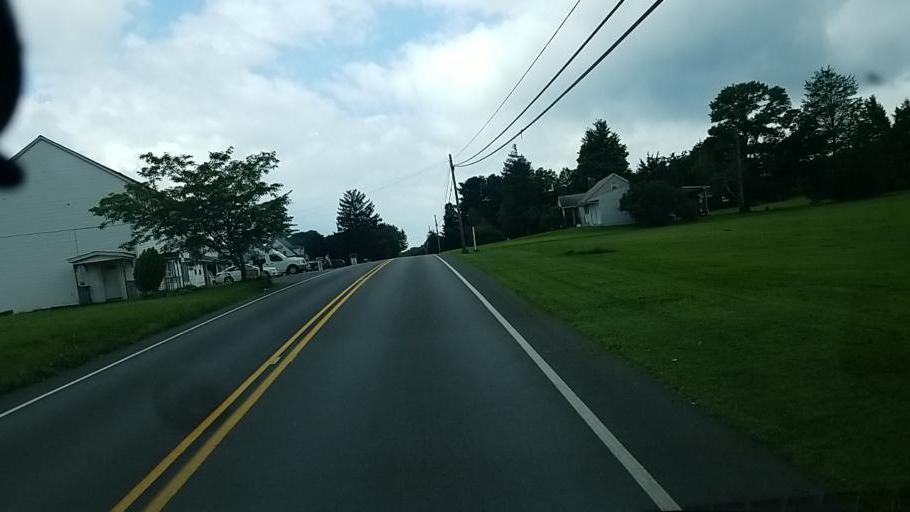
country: US
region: Pennsylvania
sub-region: Dauphin County
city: Elizabethville
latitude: 40.5147
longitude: -76.8620
